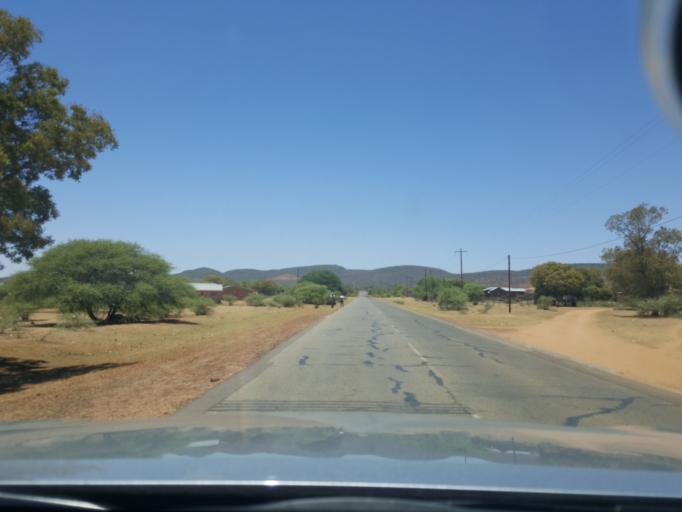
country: BW
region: South East
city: Lobatse
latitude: -25.2736
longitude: 25.9233
